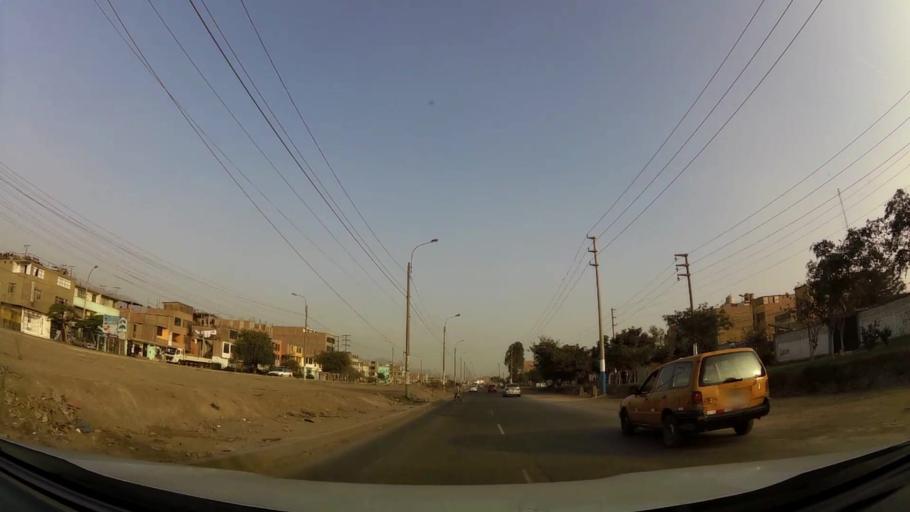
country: PE
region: Lima
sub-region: Lima
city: Independencia
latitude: -11.9481
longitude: -77.0658
